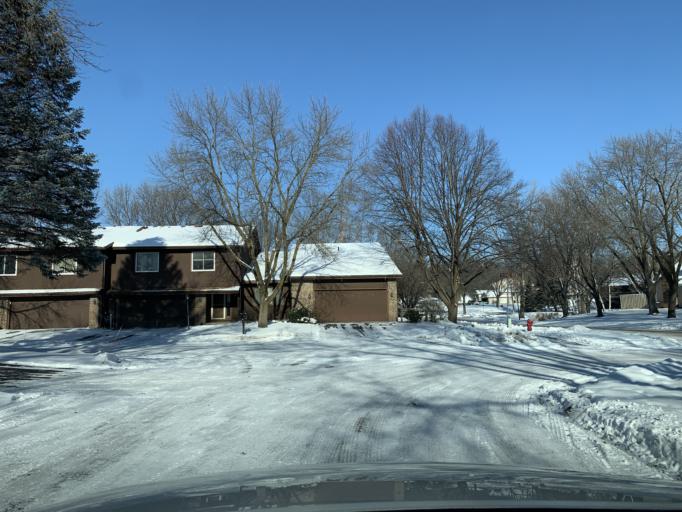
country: US
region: Minnesota
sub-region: Hennepin County
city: Edina
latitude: 44.8344
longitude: -93.3593
